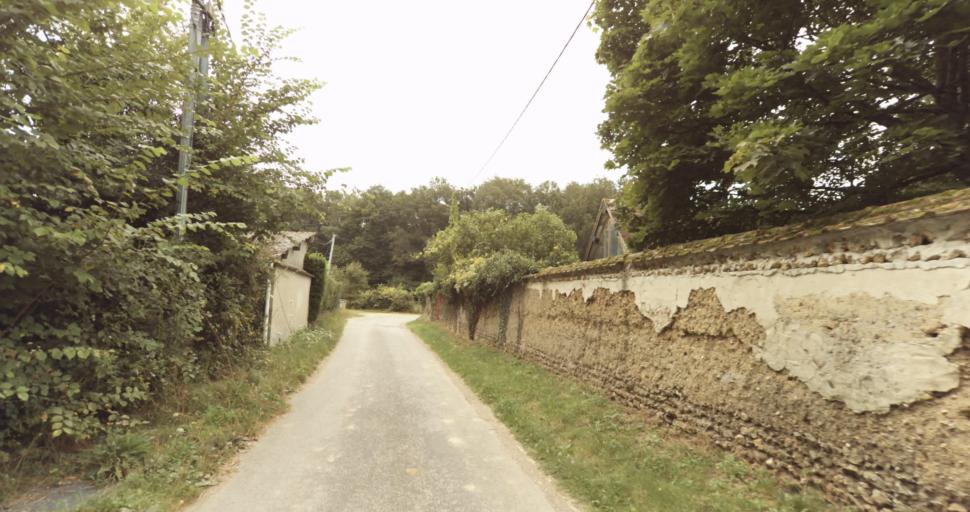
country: FR
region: Centre
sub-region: Departement d'Eure-et-Loir
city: Vert-en-Drouais
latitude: 48.7944
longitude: 1.2926
